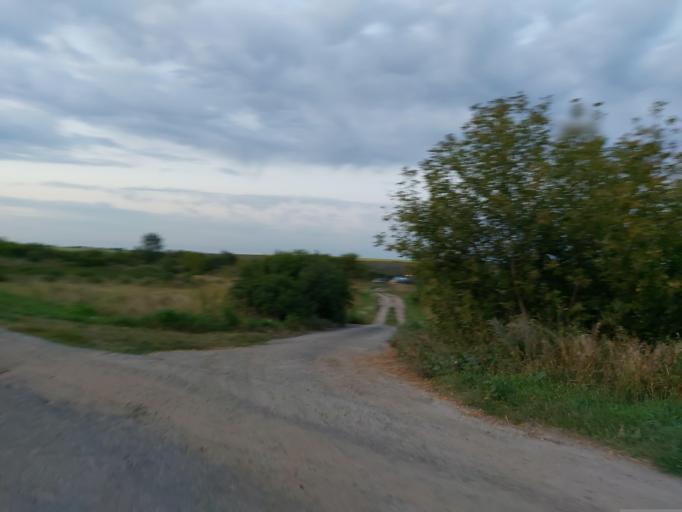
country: RU
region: Lipetsk
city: Dolgorukovo
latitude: 52.3732
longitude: 38.0538
